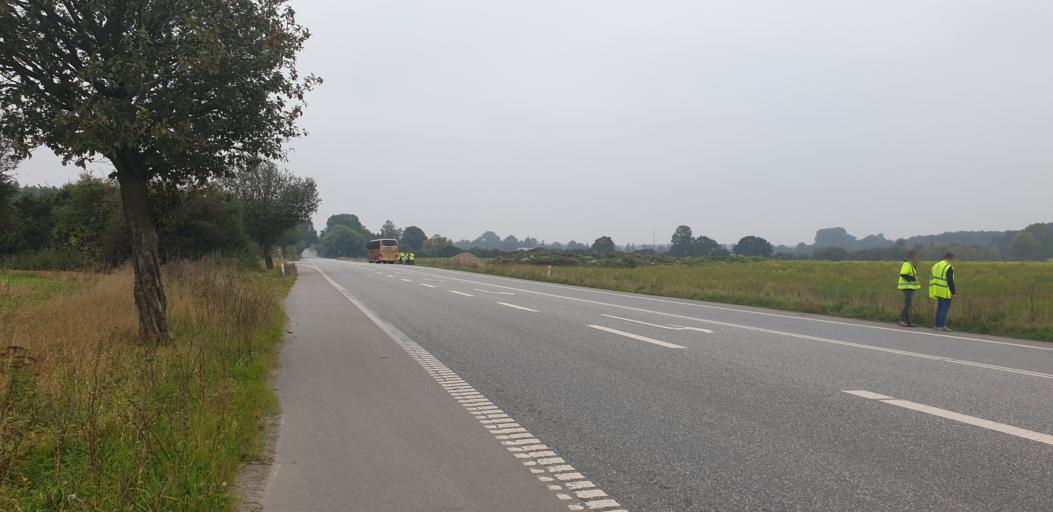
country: DK
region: Zealand
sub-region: Koge Kommune
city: Bjaeverskov
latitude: 55.3831
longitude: 12.1047
